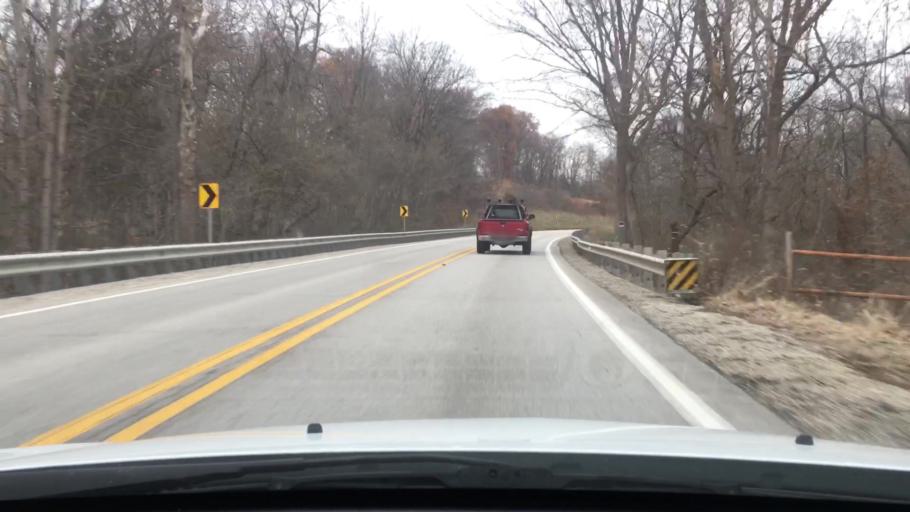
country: US
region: Missouri
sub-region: Pike County
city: Louisiana
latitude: 39.5205
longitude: -90.9478
